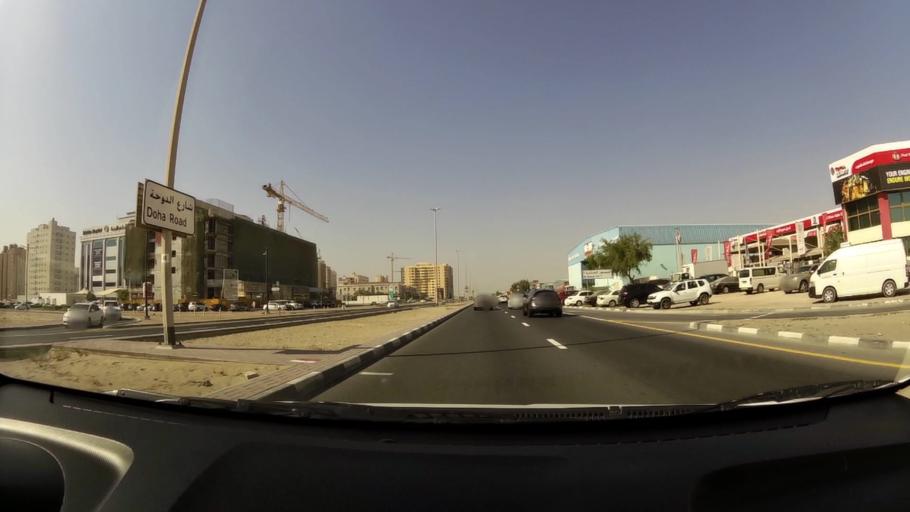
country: AE
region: Ash Shariqah
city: Sharjah
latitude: 25.2901
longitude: 55.3847
